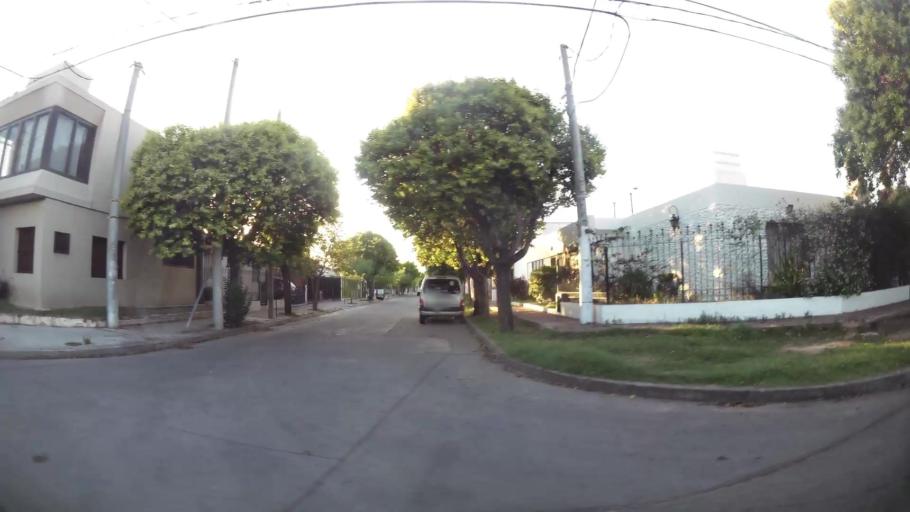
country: AR
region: Cordoba
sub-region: Departamento de Capital
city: Cordoba
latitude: -31.3775
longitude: -64.2126
